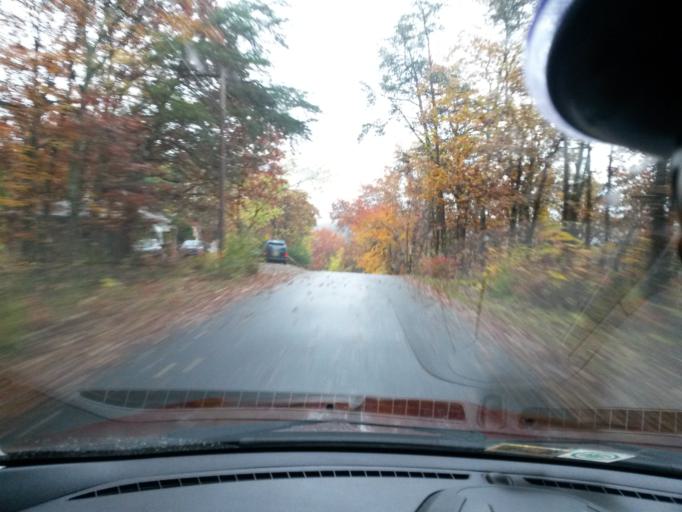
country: US
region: Virginia
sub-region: Alleghany County
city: Clifton Forge
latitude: 37.8180
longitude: -79.8182
